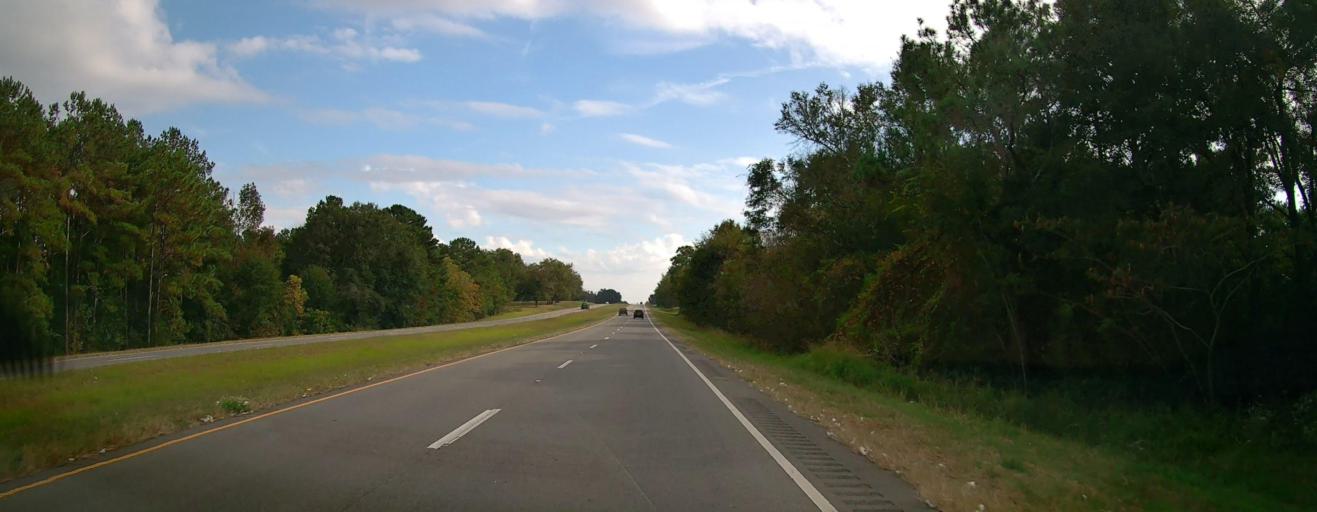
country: US
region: Georgia
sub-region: Thomas County
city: Meigs
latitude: 31.0405
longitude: -84.0675
